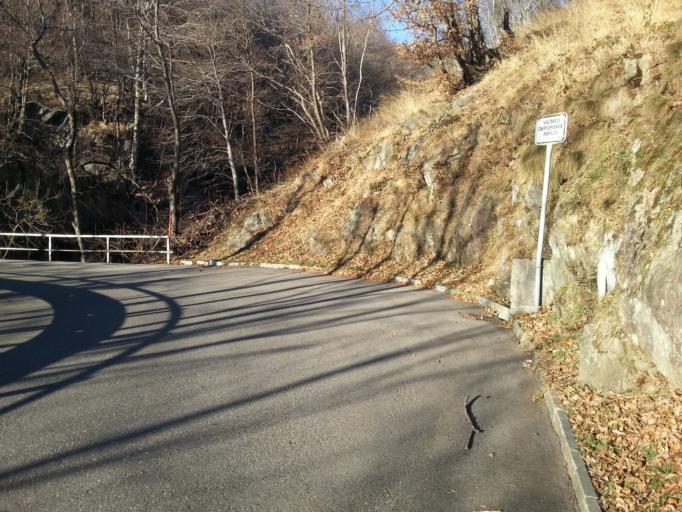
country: CH
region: Ticino
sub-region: Bellinzona District
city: Cadenazzo
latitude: 46.1206
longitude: 8.9631
